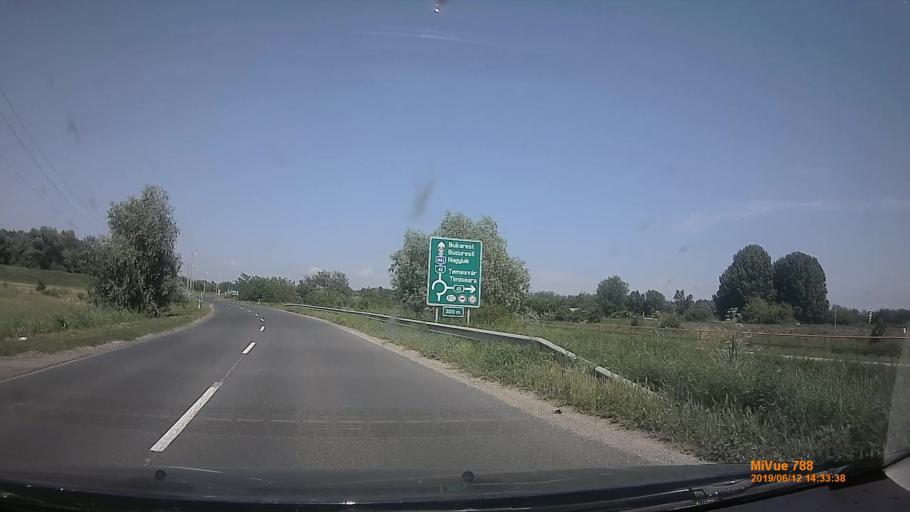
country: HU
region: Csongrad
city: Kiszombor
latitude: 46.1959
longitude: 20.4419
